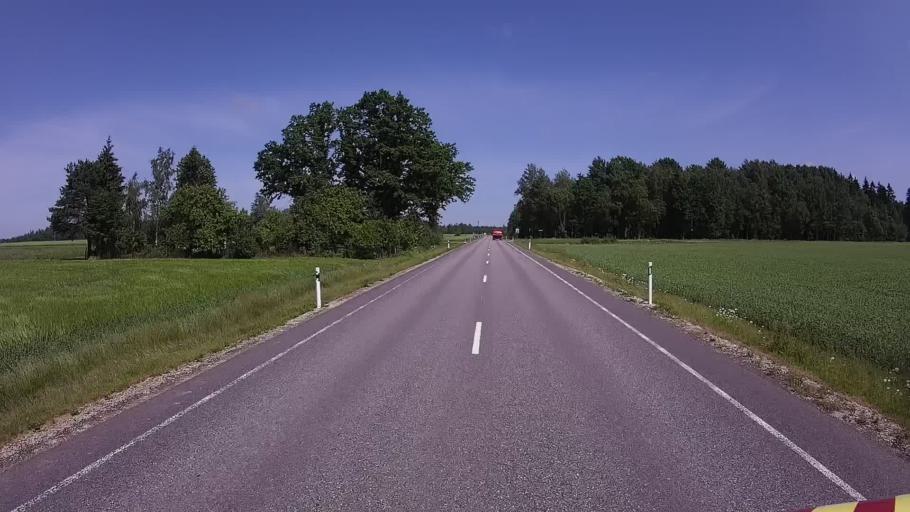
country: EE
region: Tartu
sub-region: Tartu linn
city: Tartu
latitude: 58.3921
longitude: 26.8922
